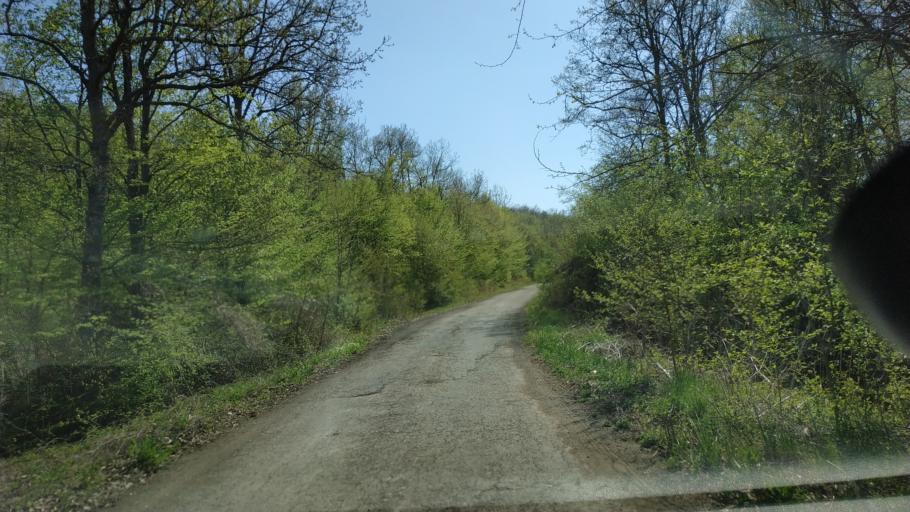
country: RS
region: Central Serbia
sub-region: Zajecarski Okrug
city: Soko Banja
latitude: 43.5082
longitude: 21.8998
